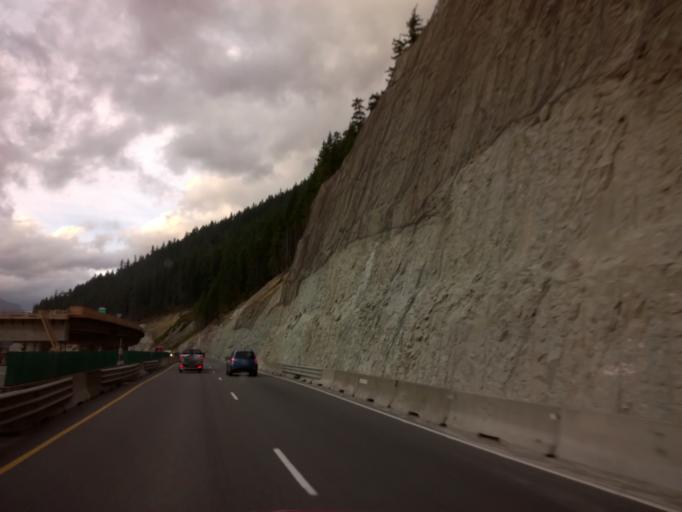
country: US
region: Washington
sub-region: King County
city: Tanner
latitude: 47.3537
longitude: -121.3652
